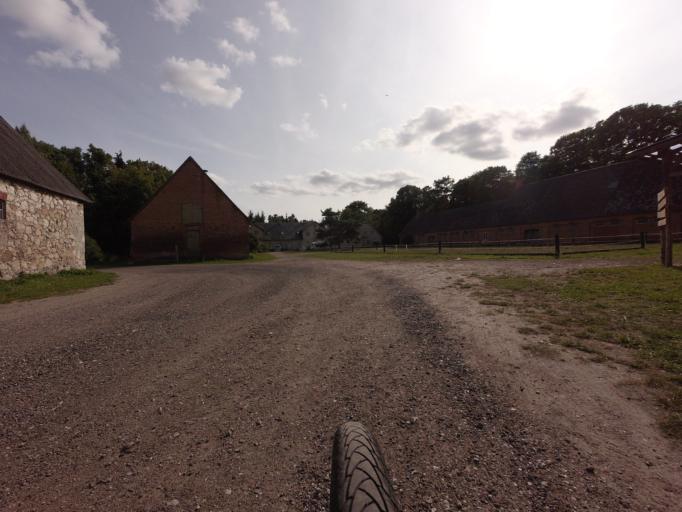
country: DK
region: Zealand
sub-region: Vordingborg Kommune
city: Praesto
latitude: 55.1582
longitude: 12.0927
